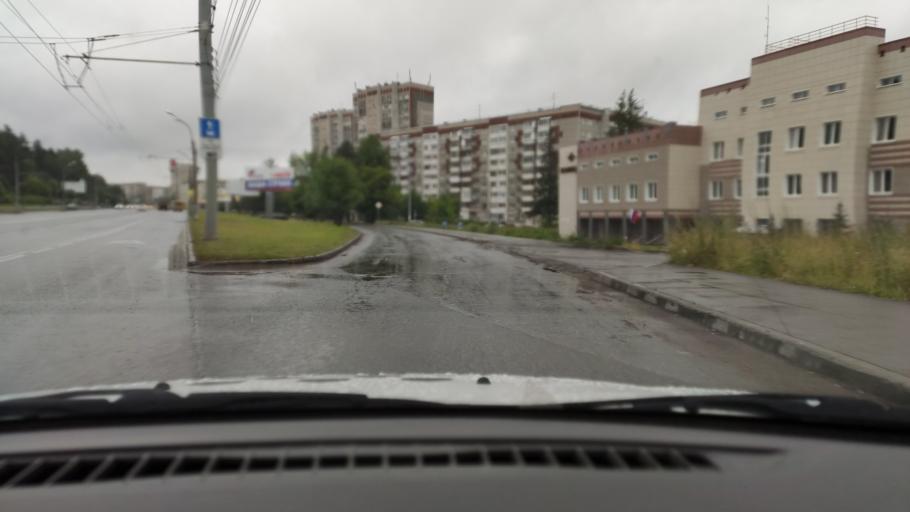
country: RU
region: Udmurtiya
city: Izhevsk
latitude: 56.8821
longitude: 53.2247
